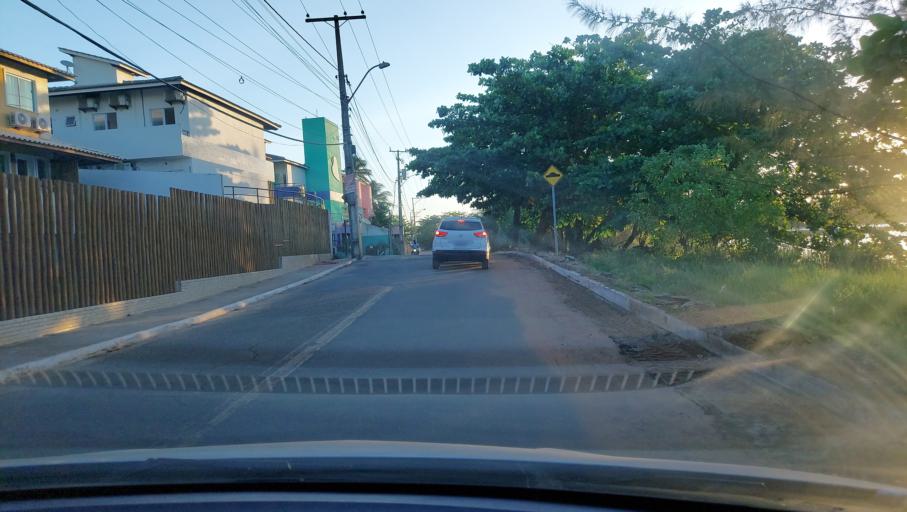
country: BR
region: Bahia
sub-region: Mata De Sao Joao
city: Mata de Sao Joao
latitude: -12.6090
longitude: -38.0419
